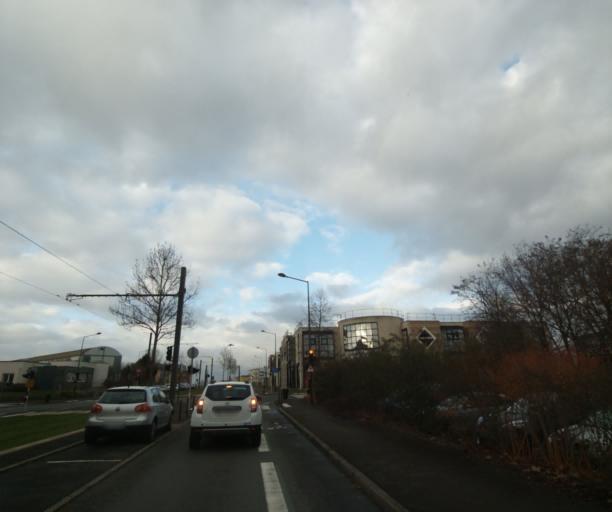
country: FR
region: Pays de la Loire
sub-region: Departement de la Sarthe
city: La Chapelle-Saint-Aubin
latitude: 48.0183
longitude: 0.1615
